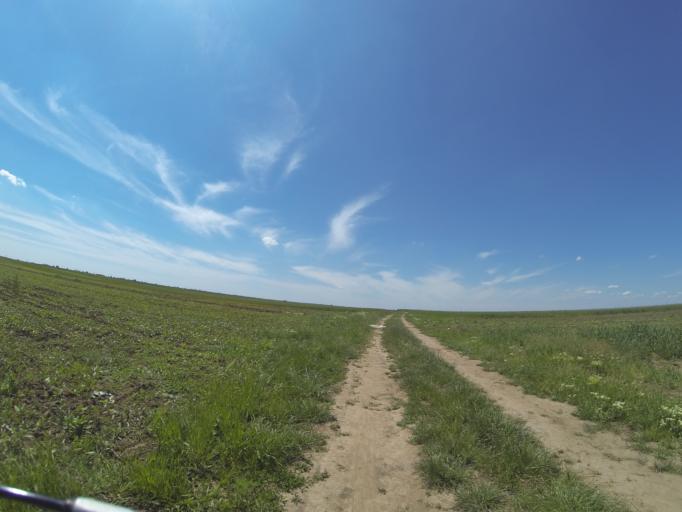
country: RO
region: Dolj
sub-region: Comuna Leu
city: Leu
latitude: 44.2169
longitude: 24.0177
